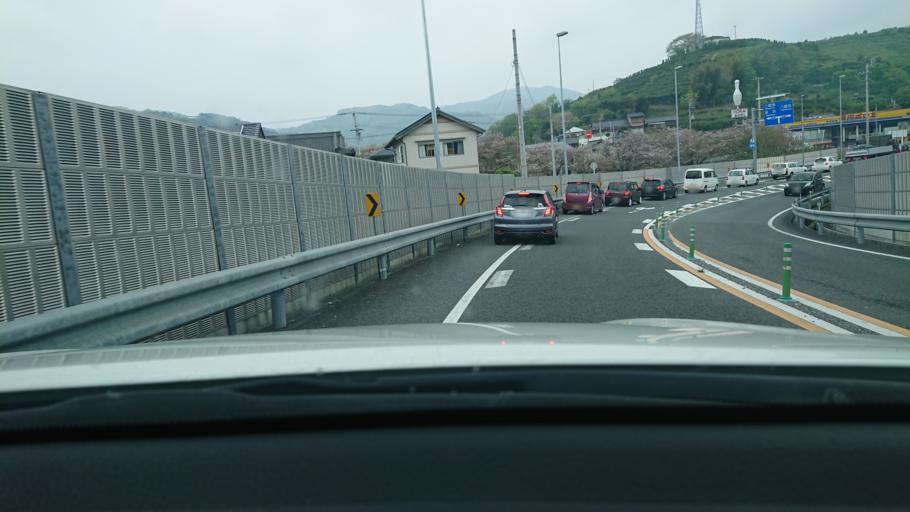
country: JP
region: Ehime
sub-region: Nishiuwa-gun
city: Ikata-cho
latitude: 33.4823
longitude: 132.4050
